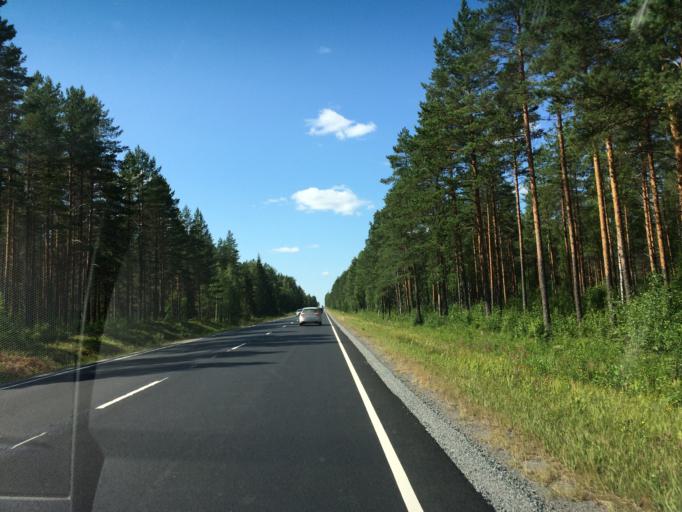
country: FI
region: Pirkanmaa
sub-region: Lounais-Pirkanmaa
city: Kiikoinen
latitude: 61.4733
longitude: 22.5050
